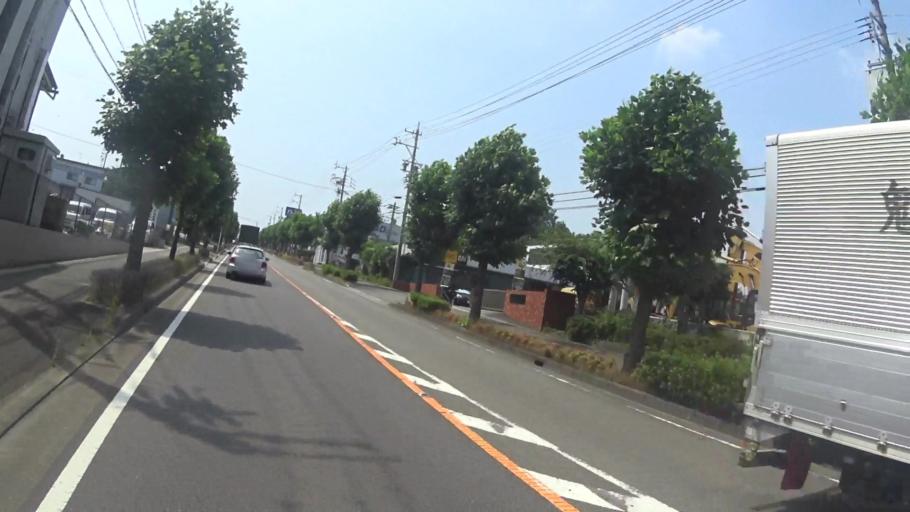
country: JP
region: Mie
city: Kawage
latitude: 34.8552
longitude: 136.5333
